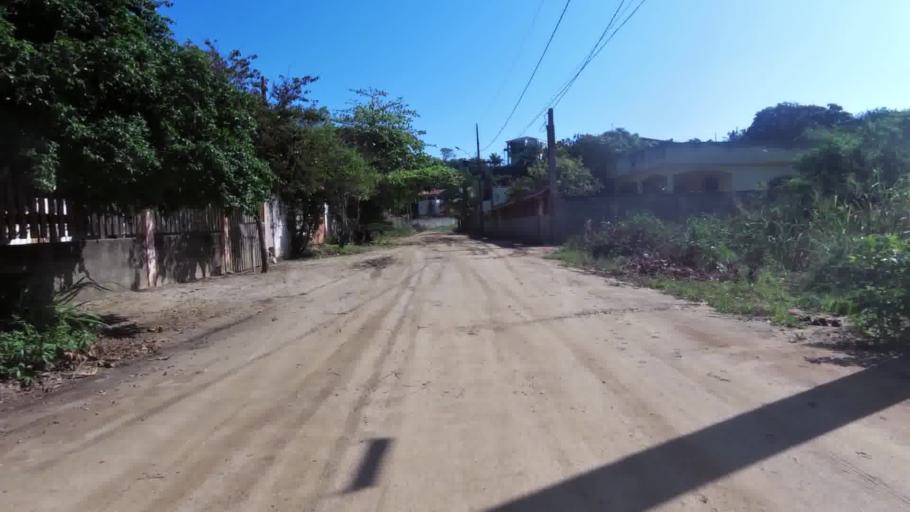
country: BR
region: Espirito Santo
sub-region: Piuma
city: Piuma
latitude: -20.8266
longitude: -40.6190
